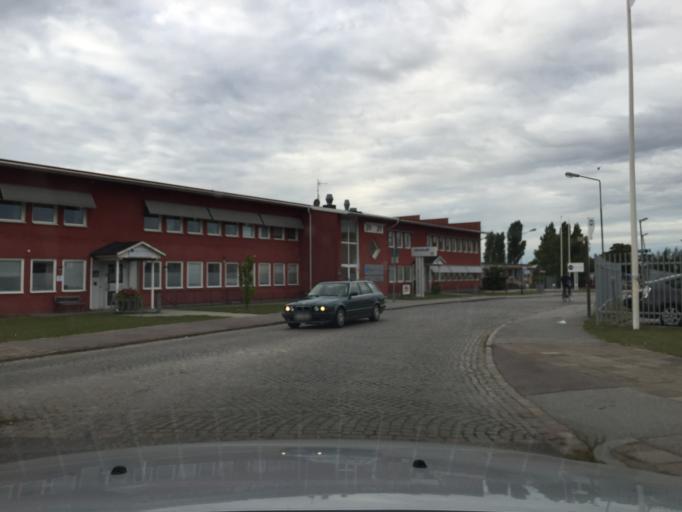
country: SE
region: Skane
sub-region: Malmo
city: Malmoe
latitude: 55.6011
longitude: 13.0398
